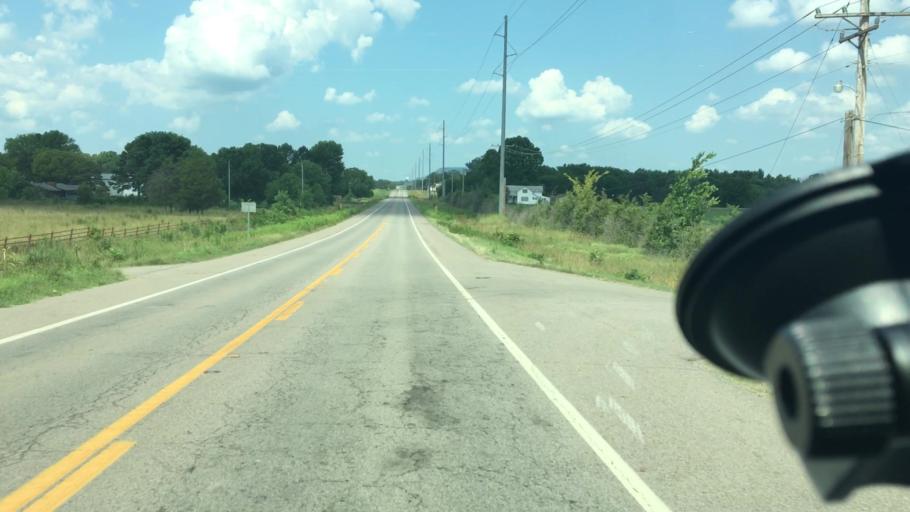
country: US
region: Arkansas
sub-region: Logan County
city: Paris
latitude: 35.2945
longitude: -93.6510
